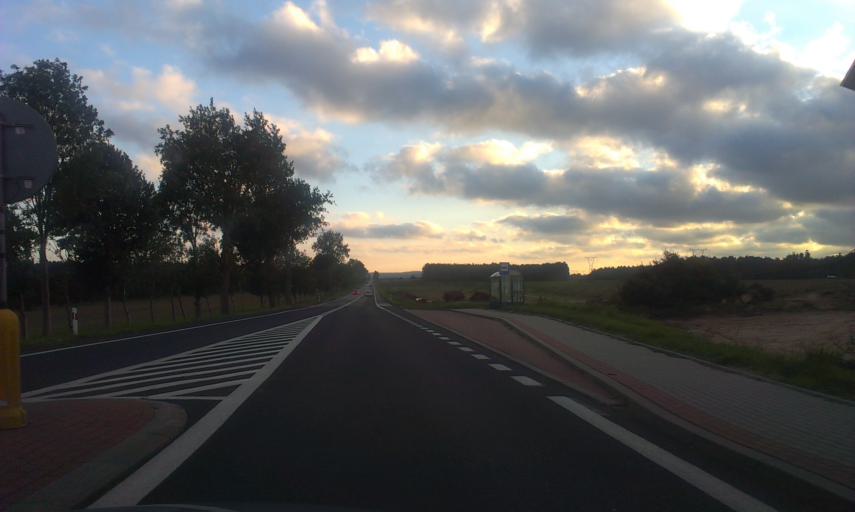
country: PL
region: West Pomeranian Voivodeship
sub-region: Powiat koszalinski
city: Sianow
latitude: 54.2490
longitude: 16.3516
